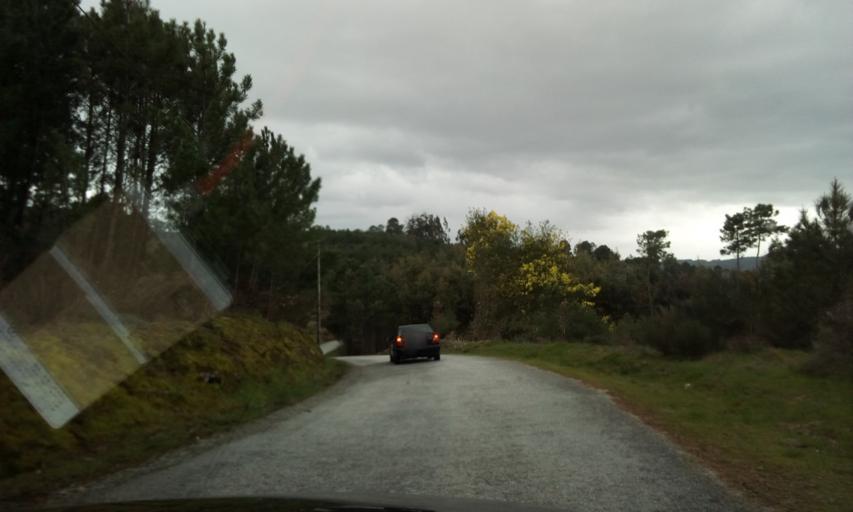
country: PT
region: Guarda
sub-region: Fornos de Algodres
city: Fornos de Algodres
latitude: 40.6368
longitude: -7.5749
